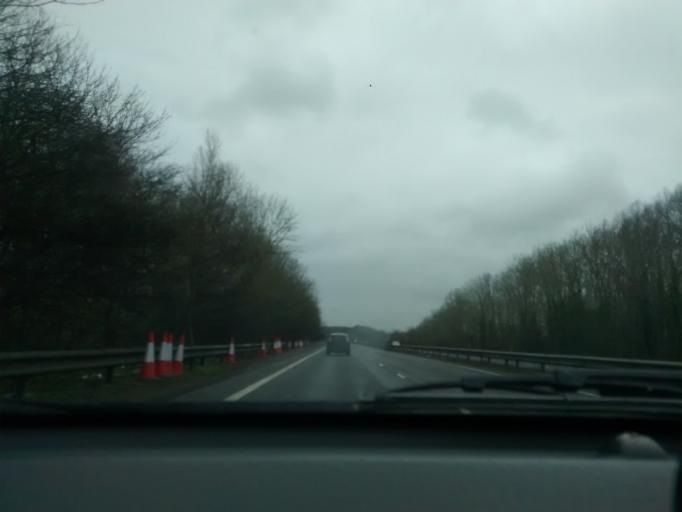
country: GB
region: England
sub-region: Suffolk
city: Needham Market
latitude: 52.1694
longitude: 1.0545
